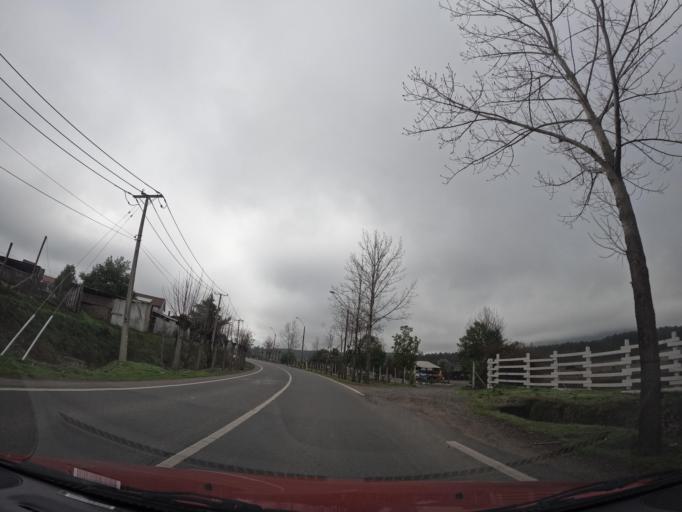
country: CL
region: Maule
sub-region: Provincia de Cauquenes
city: Cauquenes
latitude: -36.2749
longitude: -72.5410
